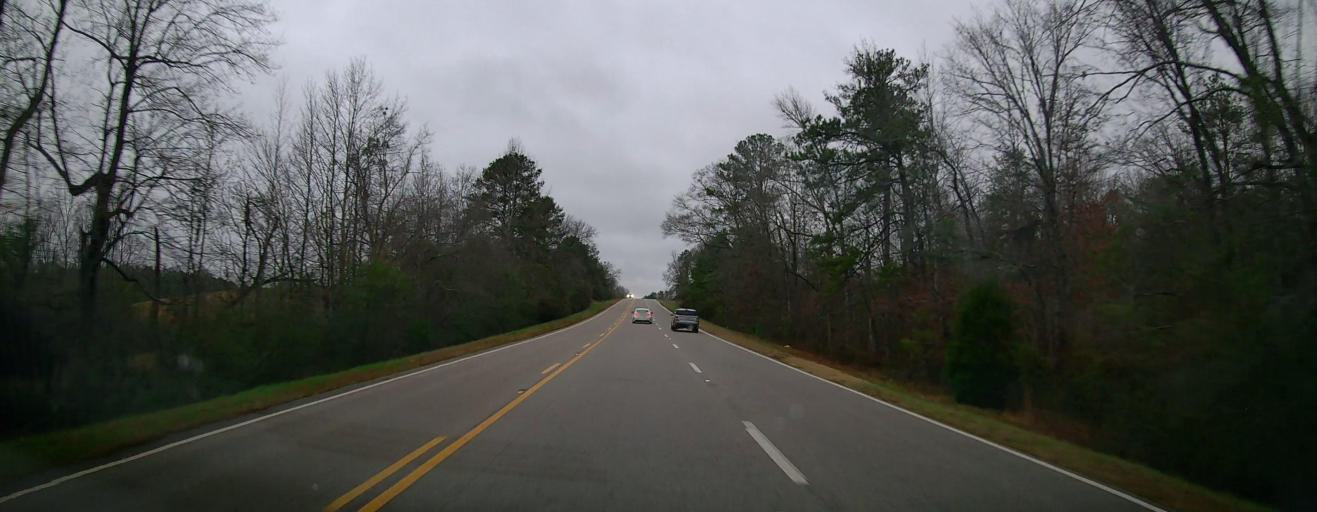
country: US
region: Alabama
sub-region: Bibb County
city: Centreville
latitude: 32.8520
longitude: -86.9630
